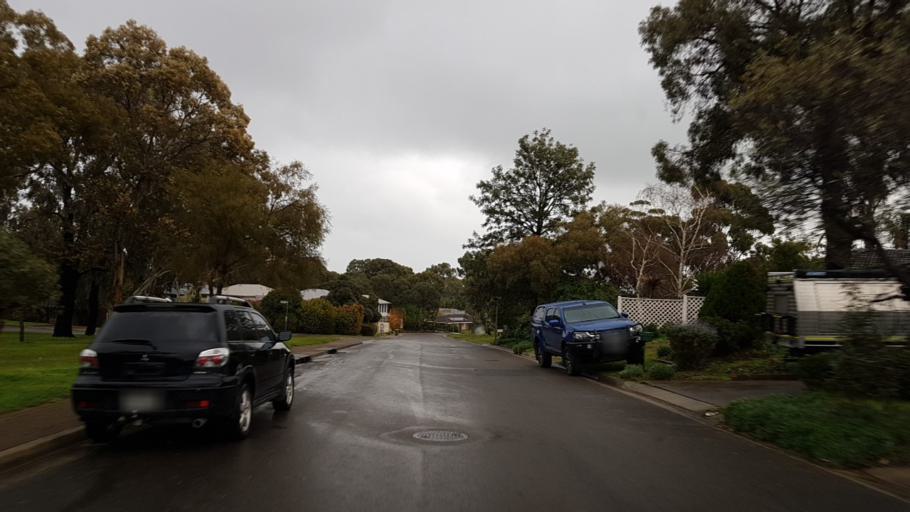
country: AU
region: South Australia
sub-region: Onkaparinga
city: Craigburn Farm
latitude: -35.0860
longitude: 138.5910
